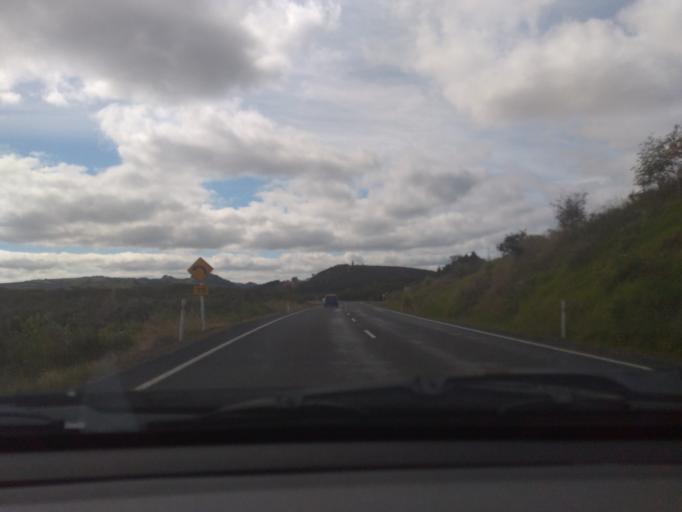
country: NZ
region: Northland
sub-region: Far North District
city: Taipa
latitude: -35.0098
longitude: 173.5417
